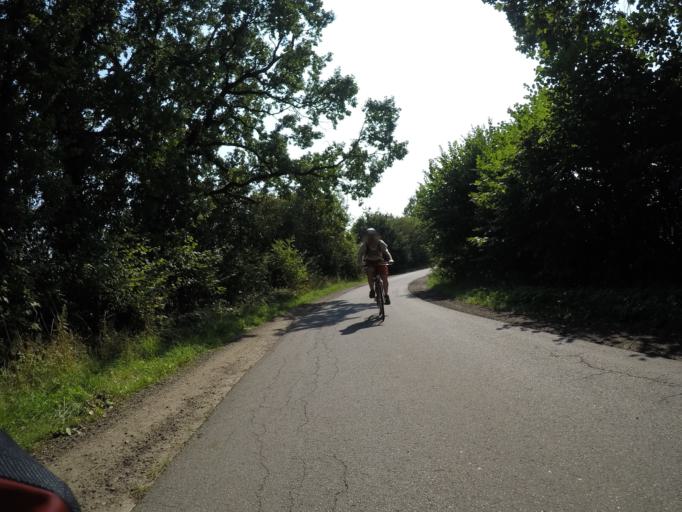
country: DE
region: Schleswig-Holstein
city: Todesfelde
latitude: 53.8848
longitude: 10.1732
